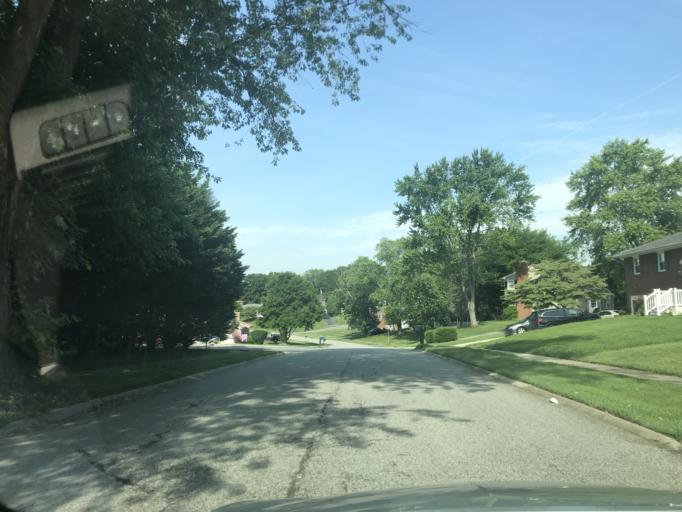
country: US
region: Maryland
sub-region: Harford County
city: Bel Air North
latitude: 39.5560
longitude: -76.3791
